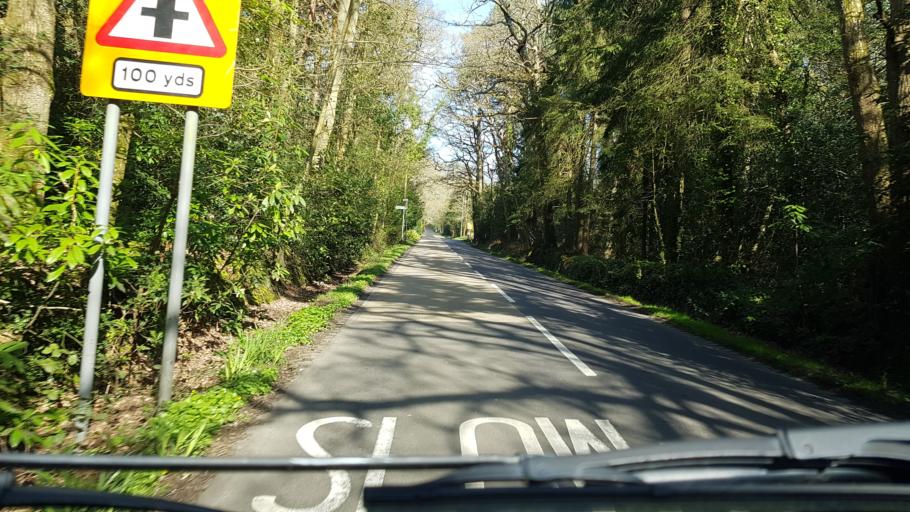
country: GB
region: England
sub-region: Surrey
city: Knaphill
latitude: 51.2976
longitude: -0.6050
